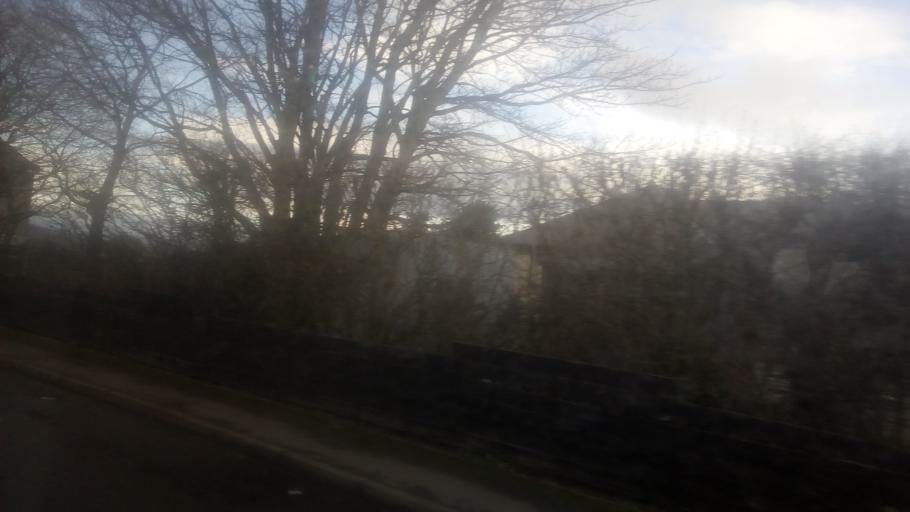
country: GB
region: Scotland
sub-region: Midlothian
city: Dalkeith
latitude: 55.8875
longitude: -3.0340
